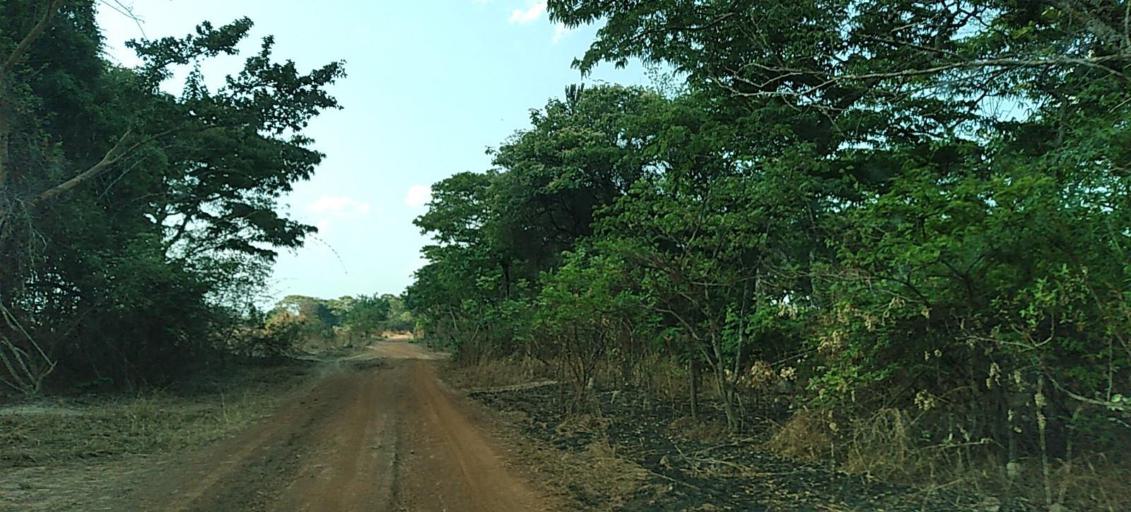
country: ZM
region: Copperbelt
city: Mpongwe
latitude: -13.4619
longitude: 28.0686
